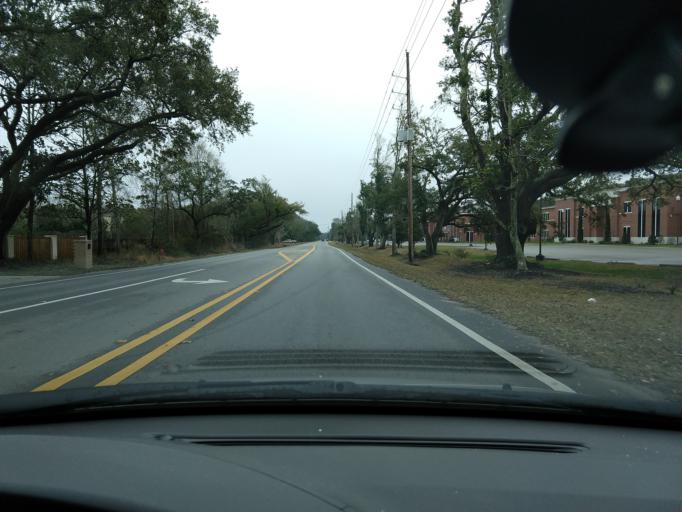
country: US
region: Mississippi
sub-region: Jackson County
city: Gulf Park Estates
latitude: 30.3956
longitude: -88.7213
